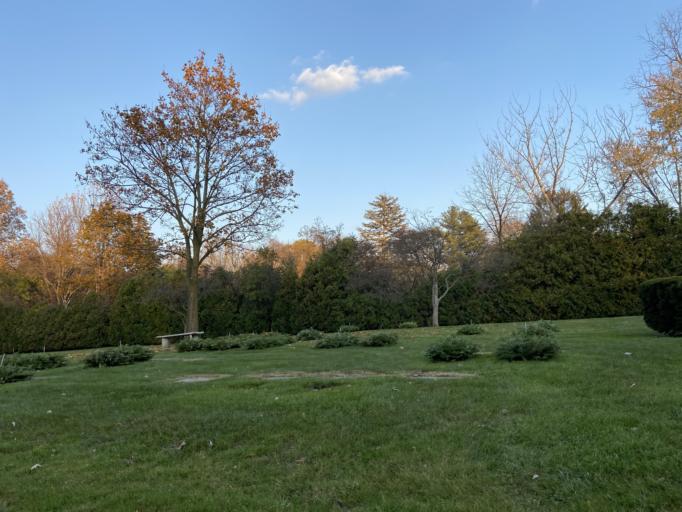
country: US
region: Michigan
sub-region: Wayne County
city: Redford
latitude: 42.4153
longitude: -83.3259
